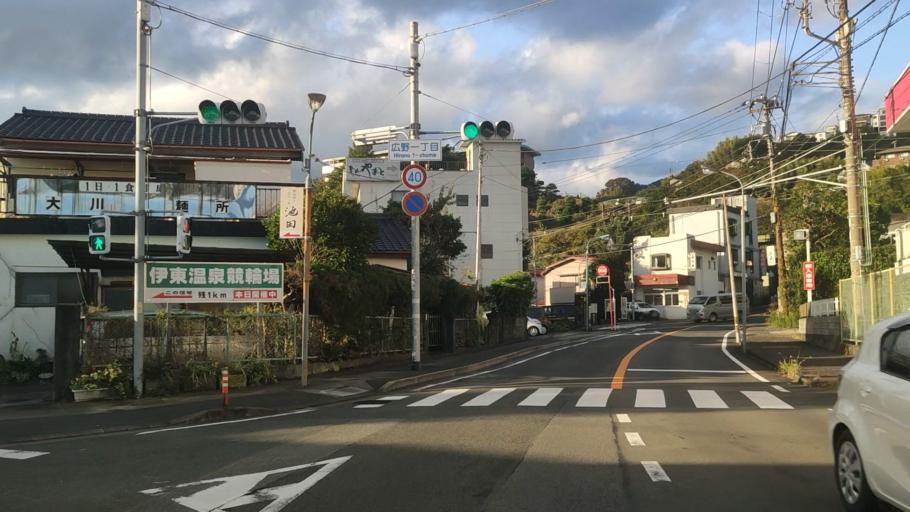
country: JP
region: Shizuoka
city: Ito
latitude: 34.9632
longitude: 139.0906
